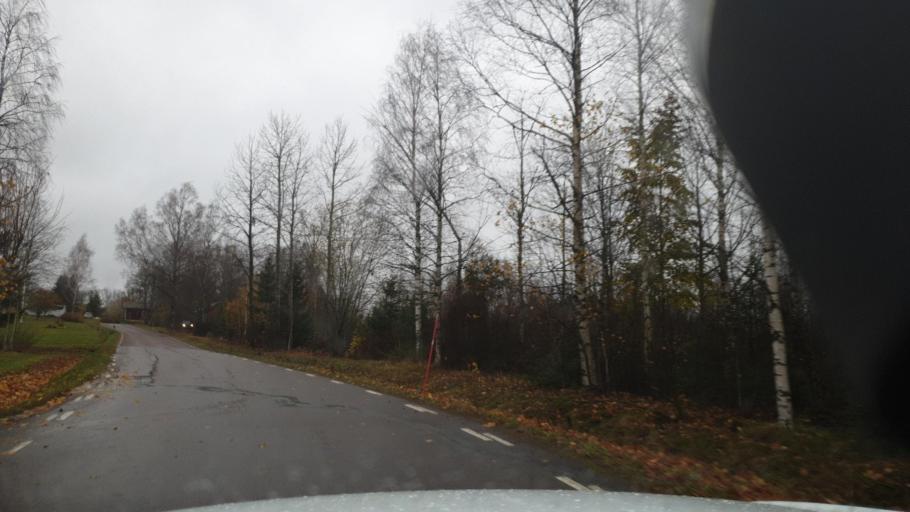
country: SE
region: Vaermland
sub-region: Sunne Kommun
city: Sunne
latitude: 59.7366
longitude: 13.1298
